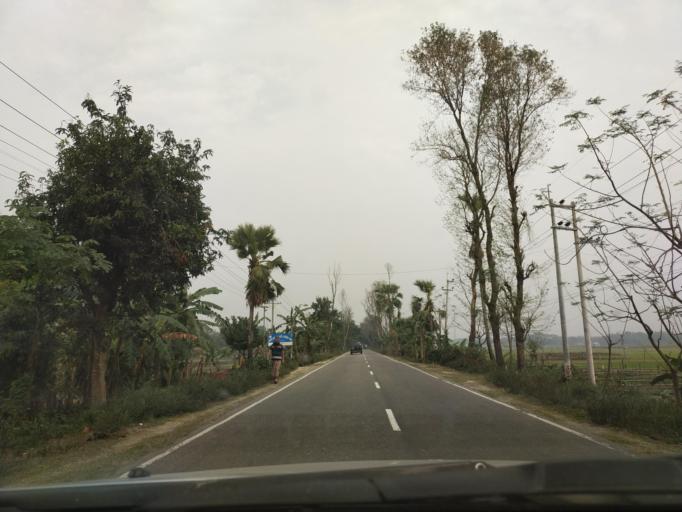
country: BD
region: Dhaka
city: Narsingdi
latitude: 23.9999
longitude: 90.7376
